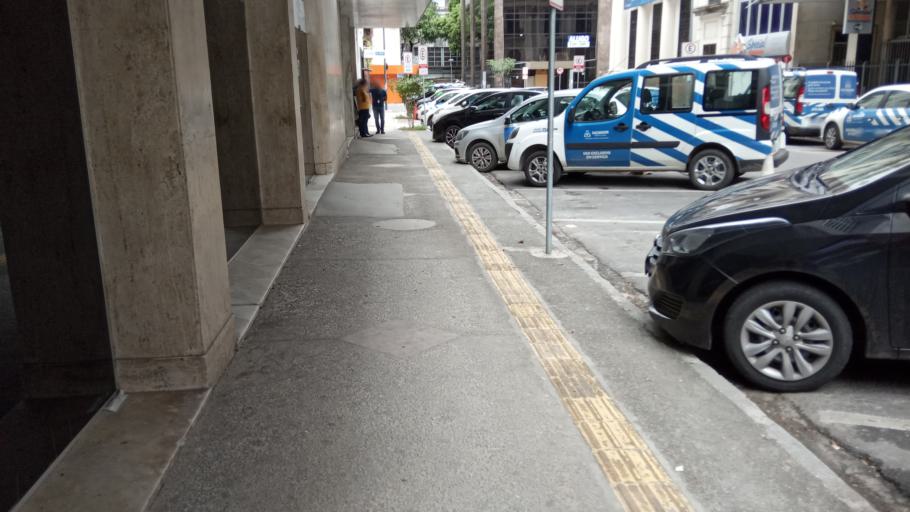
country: BR
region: Bahia
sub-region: Salvador
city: Salvador
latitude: -12.9718
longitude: -38.5137
